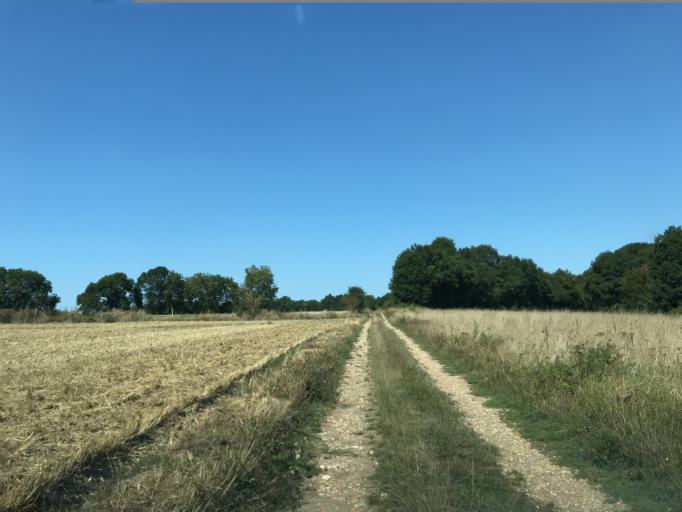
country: FR
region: Haute-Normandie
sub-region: Departement de l'Eure
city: Heudreville-sur-Eure
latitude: 49.1035
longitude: 1.2041
